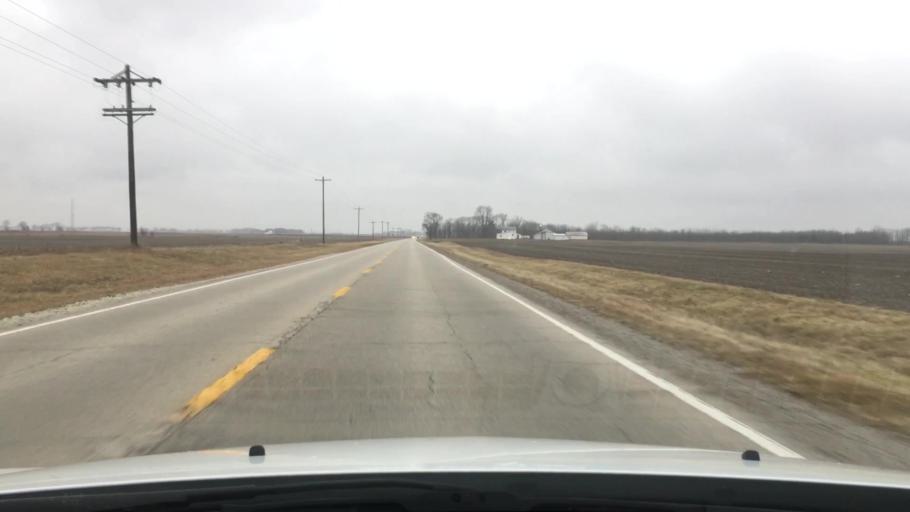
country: US
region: Illinois
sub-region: Iroquois County
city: Watseka
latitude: 40.8904
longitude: -87.7136
